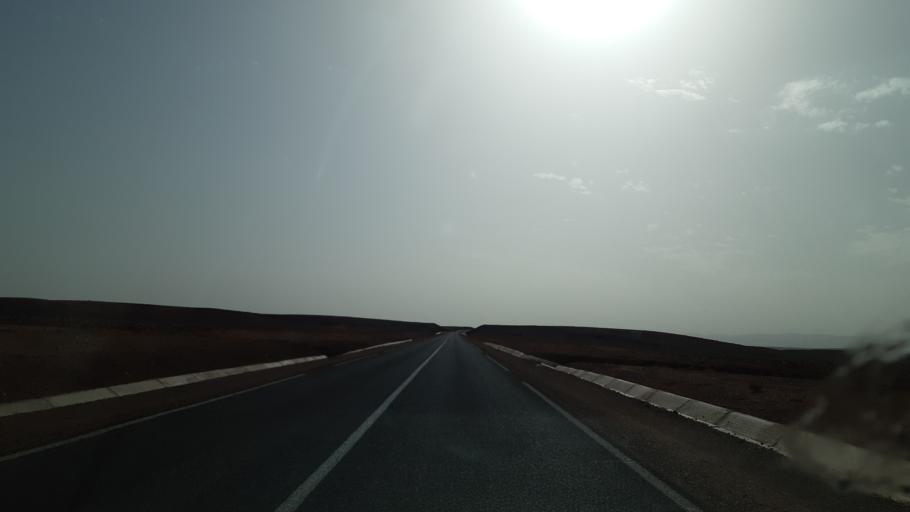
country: MA
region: Meknes-Tafilalet
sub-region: Khenifra
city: Midelt
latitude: 32.8889
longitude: -4.7464
